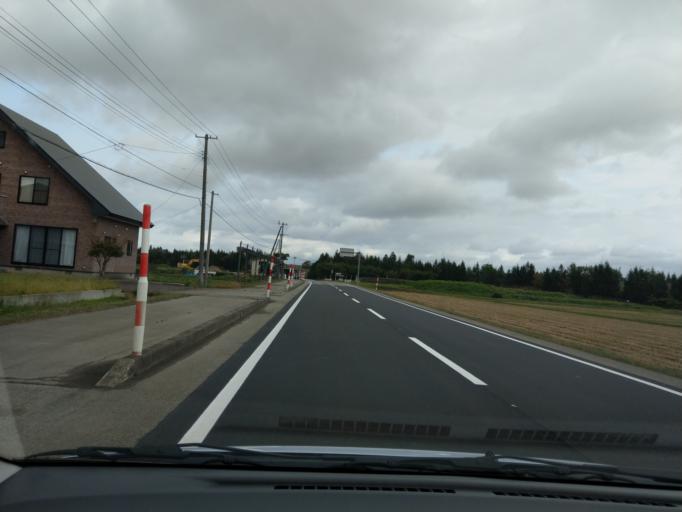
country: JP
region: Akita
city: Omagari
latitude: 39.3965
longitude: 140.4736
